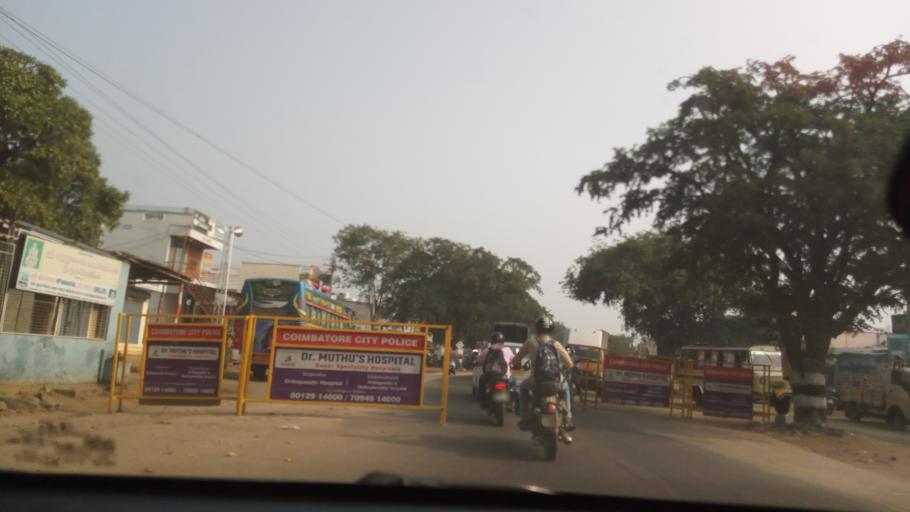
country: IN
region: Tamil Nadu
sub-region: Coimbatore
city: Annur
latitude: 11.1738
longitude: 77.0565
